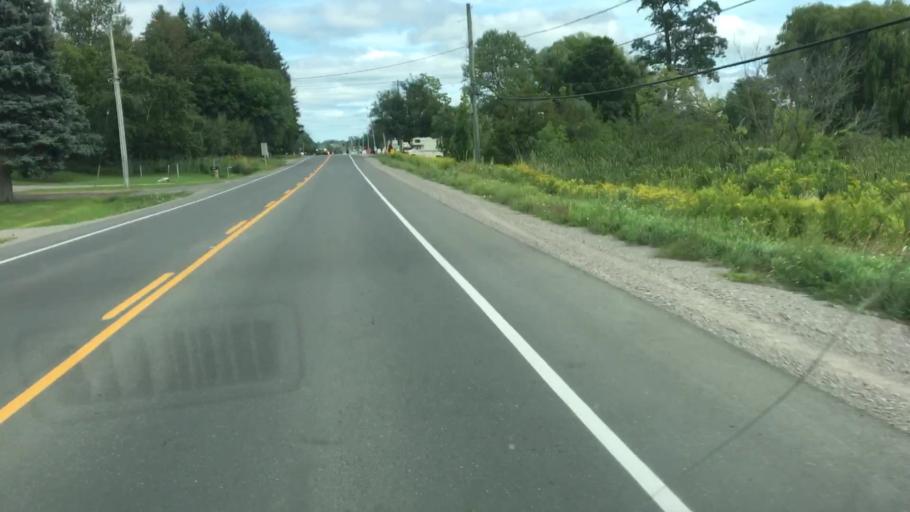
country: CA
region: Ontario
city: Quinte West
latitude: 44.0361
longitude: -77.7627
